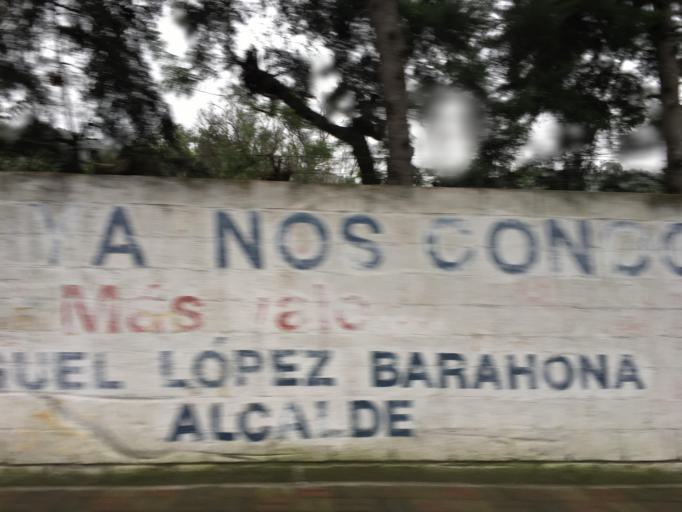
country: GT
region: Sacatepequez
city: Pastores
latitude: 14.5983
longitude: -90.7564
